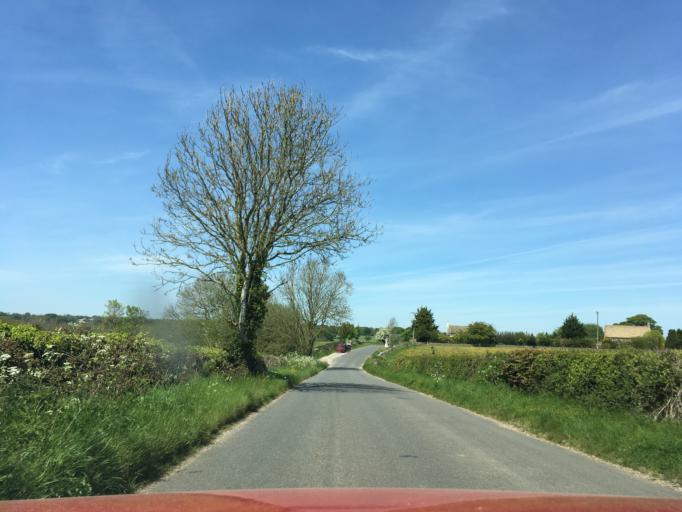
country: GB
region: England
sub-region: Gloucestershire
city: Chalford
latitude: 51.7178
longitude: -2.1172
